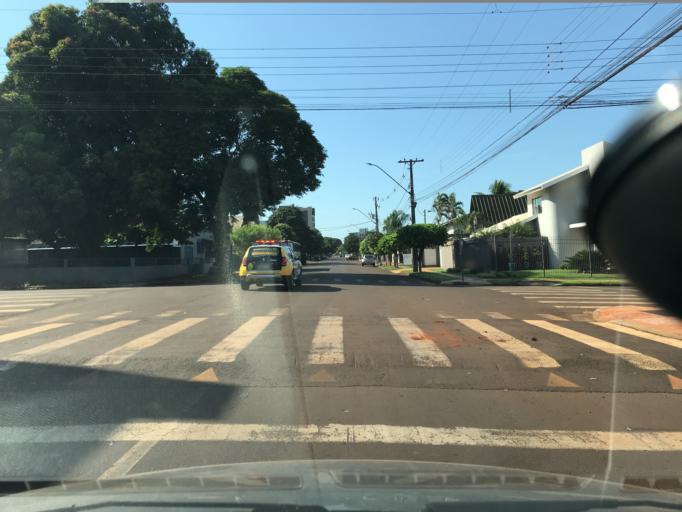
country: BR
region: Parana
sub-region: Palotina
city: Palotina
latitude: -24.2801
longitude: -53.8423
